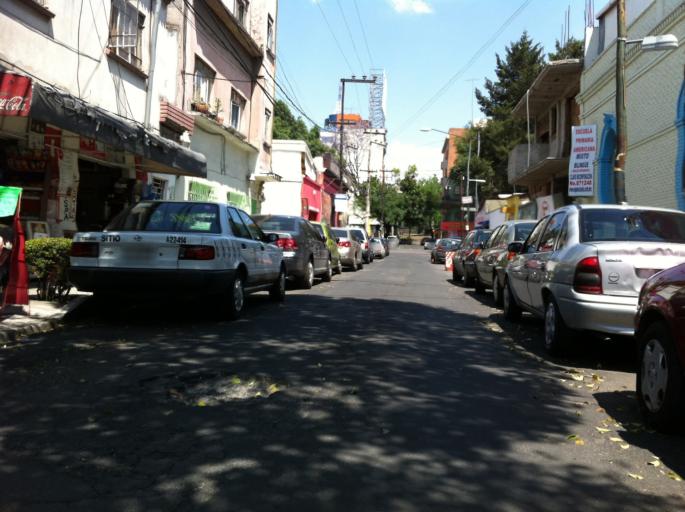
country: MX
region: Mexico City
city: Colonia del Valle
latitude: 19.3945
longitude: -99.1827
